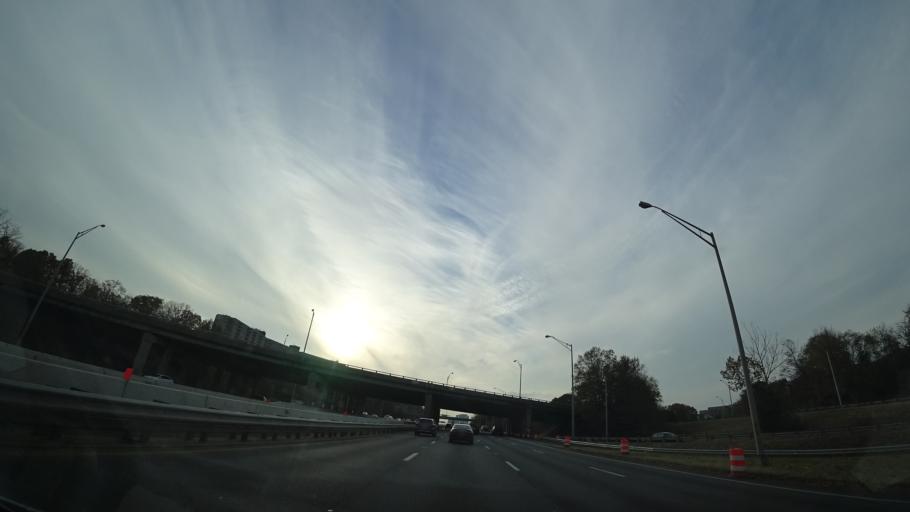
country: US
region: Virginia
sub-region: Fairfax County
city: Baileys Crossroads
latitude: 38.8351
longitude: -77.0971
